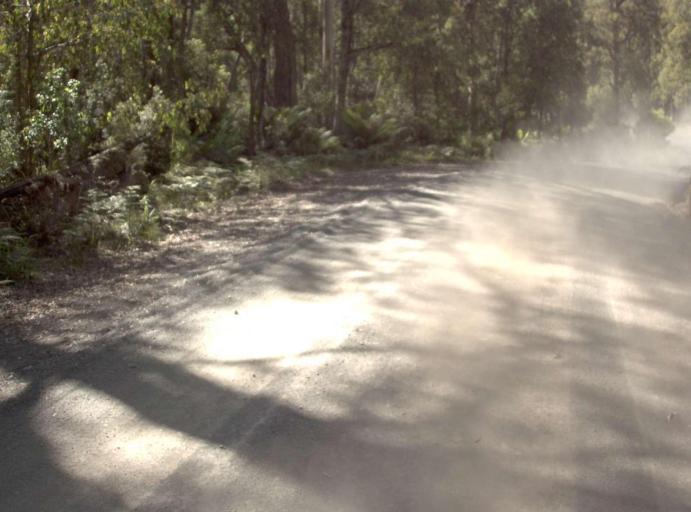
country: AU
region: New South Wales
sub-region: Bombala
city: Bombala
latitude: -37.2109
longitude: 148.7431
